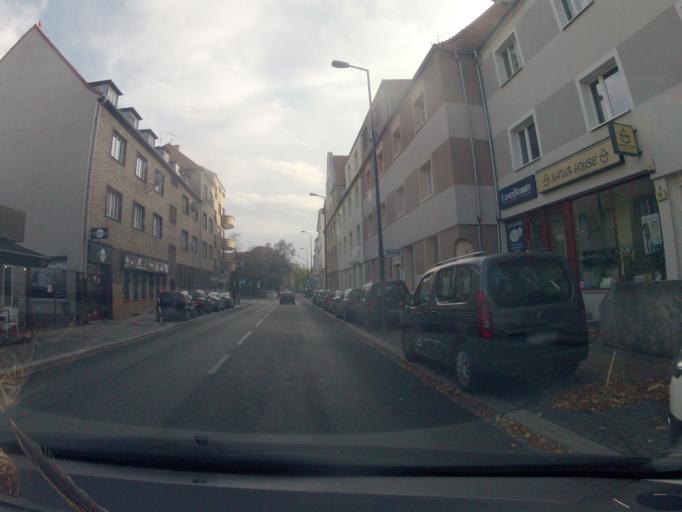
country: PL
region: Opole Voivodeship
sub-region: Powiat opolski
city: Opole
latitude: 50.6667
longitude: 17.9267
